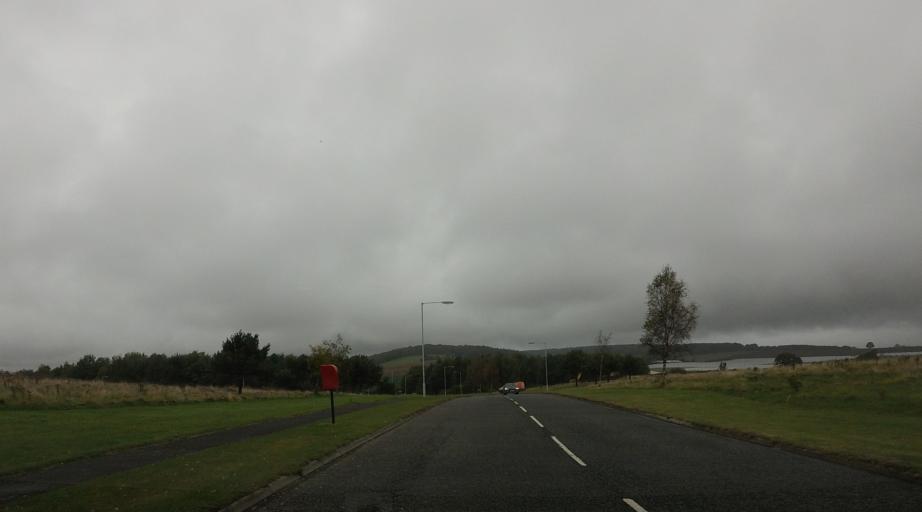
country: GB
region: Scotland
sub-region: Fife
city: Newport-On-Tay
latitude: 56.4154
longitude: -2.9140
